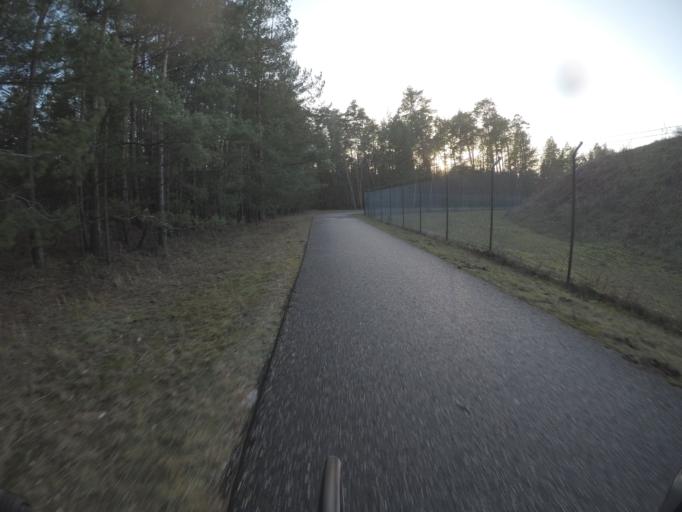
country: DE
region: Brandenburg
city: Hennigsdorf
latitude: 52.6579
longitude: 13.2252
